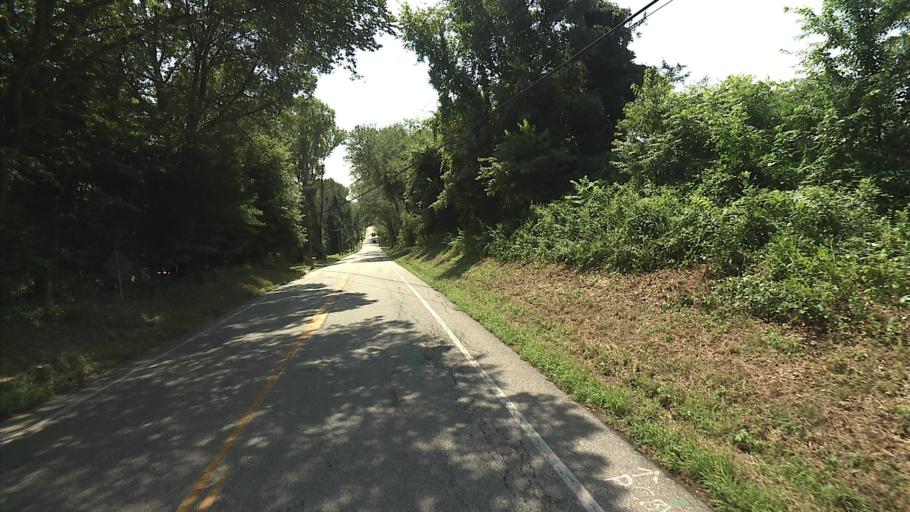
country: US
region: Connecticut
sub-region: New London County
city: Niantic
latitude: 41.3803
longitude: -72.2166
